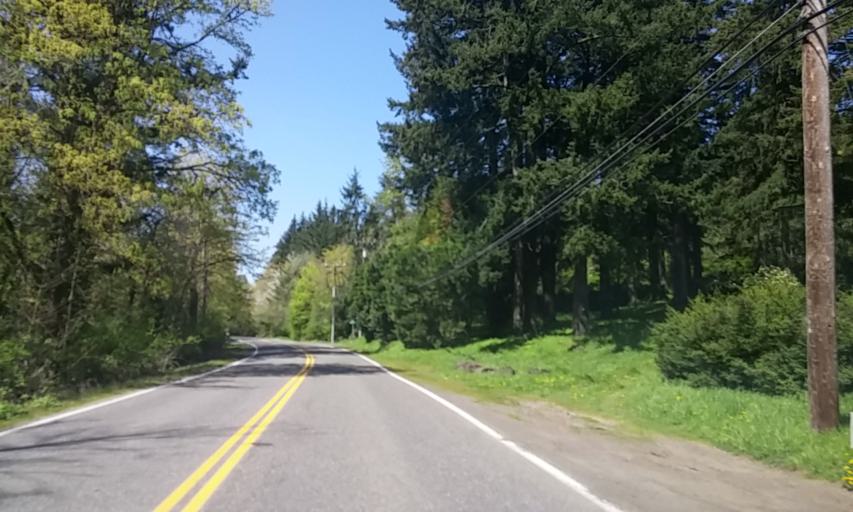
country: US
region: Oregon
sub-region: Washington County
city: West Haven-Sylvan
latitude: 45.5221
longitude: -122.7573
